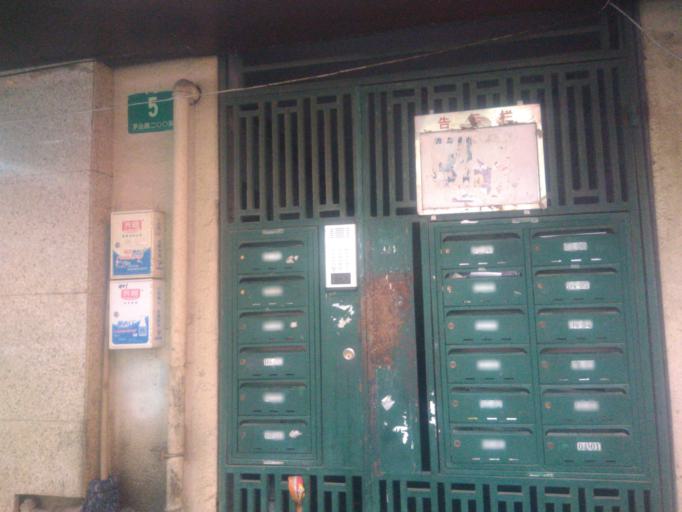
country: CN
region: Shanghai Shi
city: Changning
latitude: 31.2118
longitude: 121.3978
